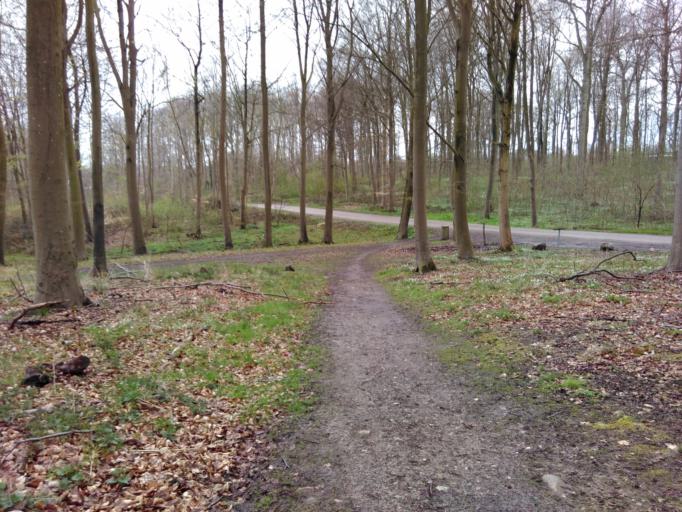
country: DK
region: South Denmark
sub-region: Faaborg-Midtfyn Kommune
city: Faaborg
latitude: 55.0744
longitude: 10.2171
